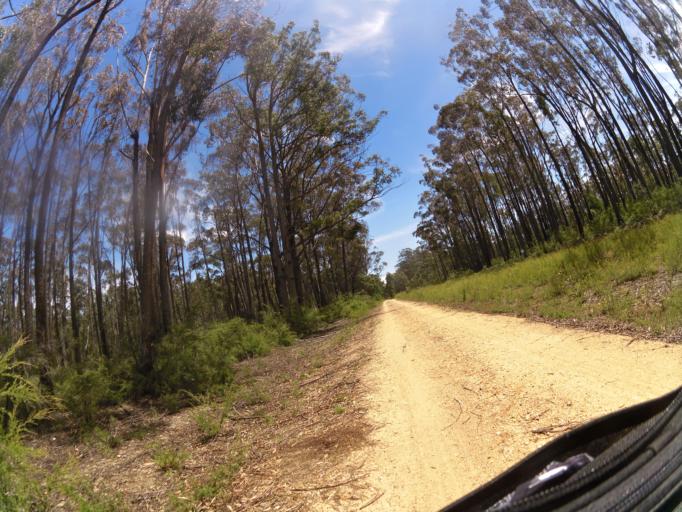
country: AU
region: Victoria
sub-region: East Gippsland
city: Lakes Entrance
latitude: -37.7588
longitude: 147.9500
